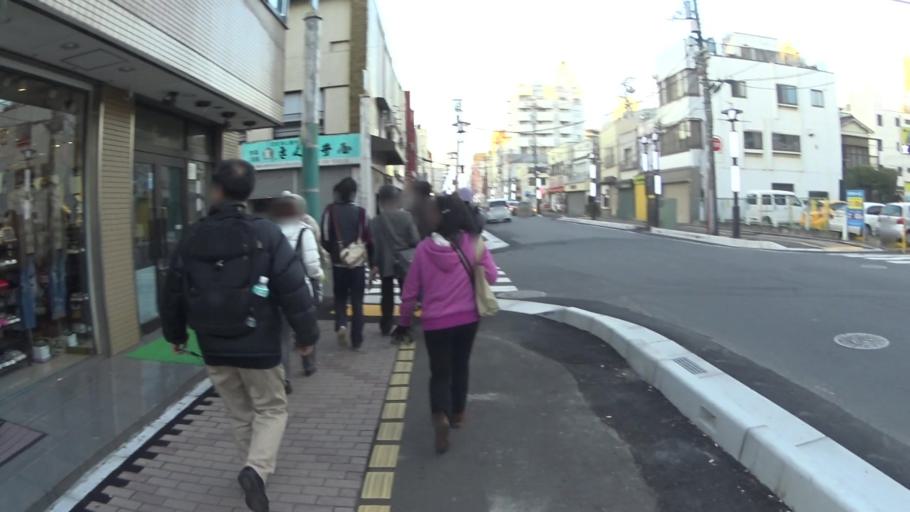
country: JP
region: Chiba
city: Chiba
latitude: 35.6123
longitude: 140.1211
